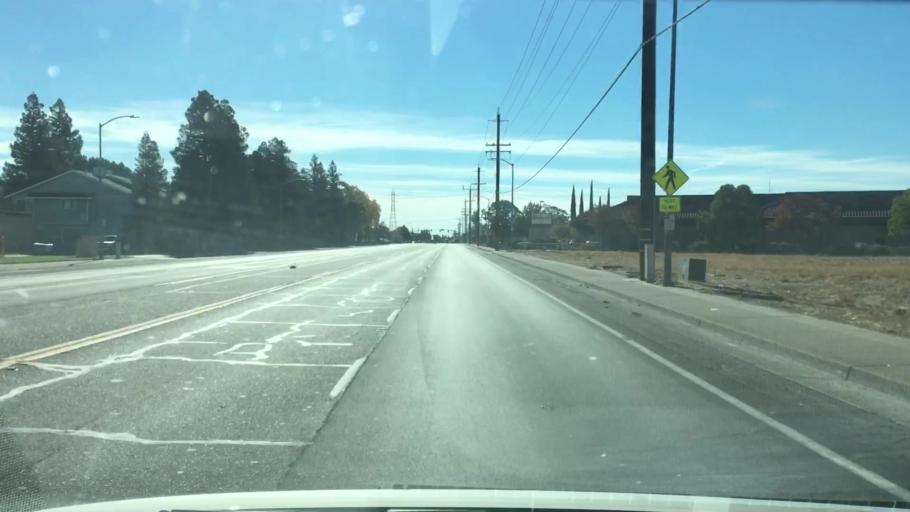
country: US
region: California
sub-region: Sacramento County
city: Florin
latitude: 38.4783
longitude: -121.4209
